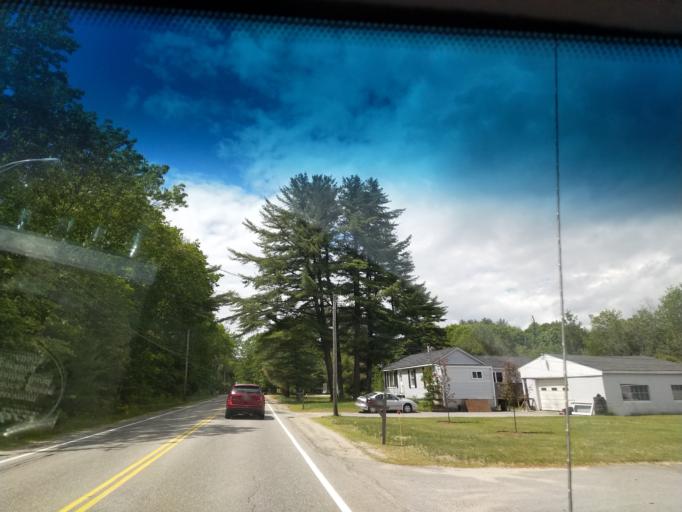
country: US
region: Maine
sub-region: Cumberland County
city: Westbrook
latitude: 43.6301
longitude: -70.3795
